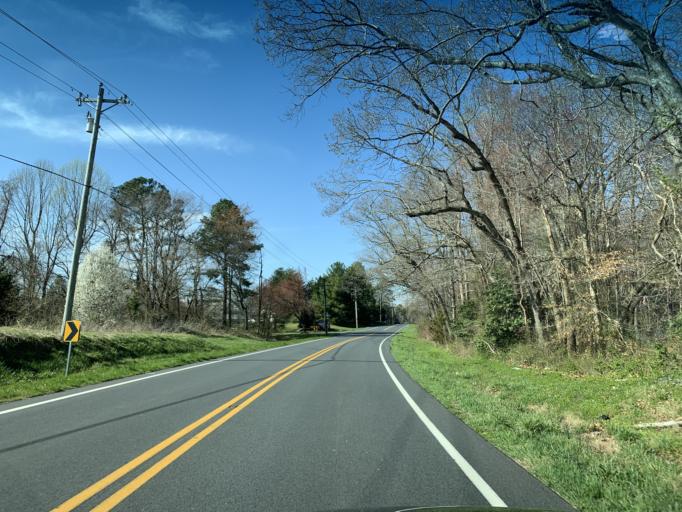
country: US
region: Delaware
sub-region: Kent County
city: Riverview
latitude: 38.9855
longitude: -75.5098
